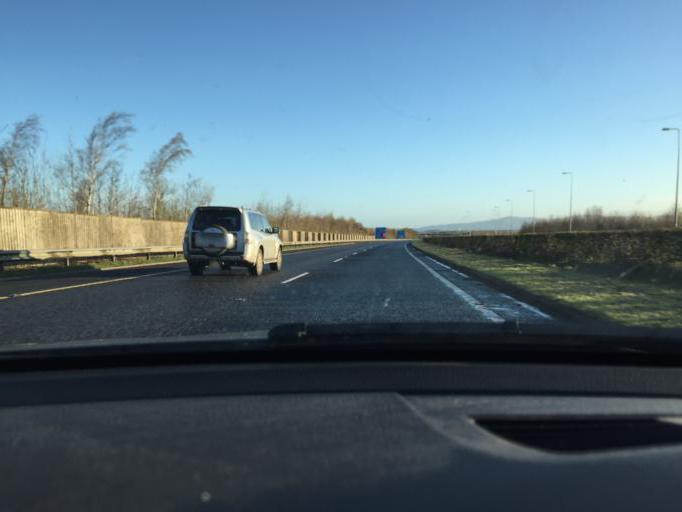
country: IE
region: Leinster
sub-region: Lu
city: Dromiskin
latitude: 53.9185
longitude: -6.4159
